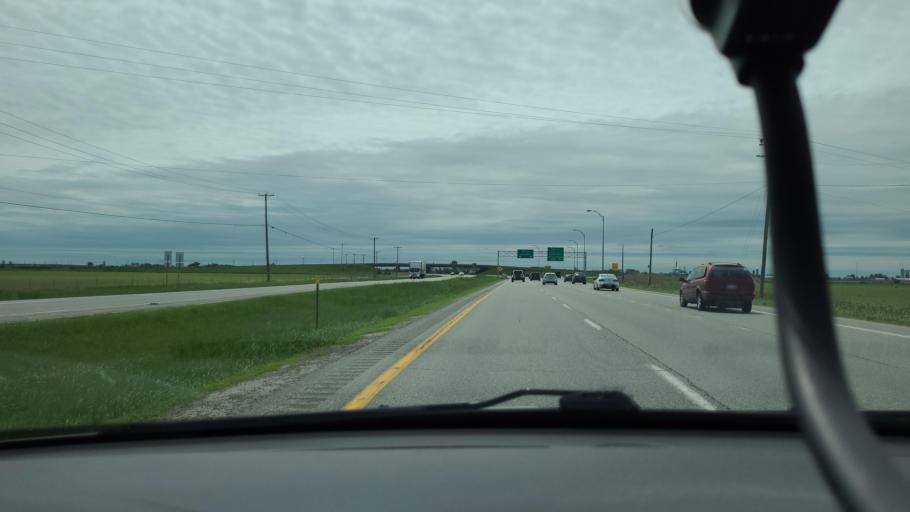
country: CA
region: Quebec
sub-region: Lanaudiere
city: Sainte-Julienne
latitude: 45.8895
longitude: -73.6608
